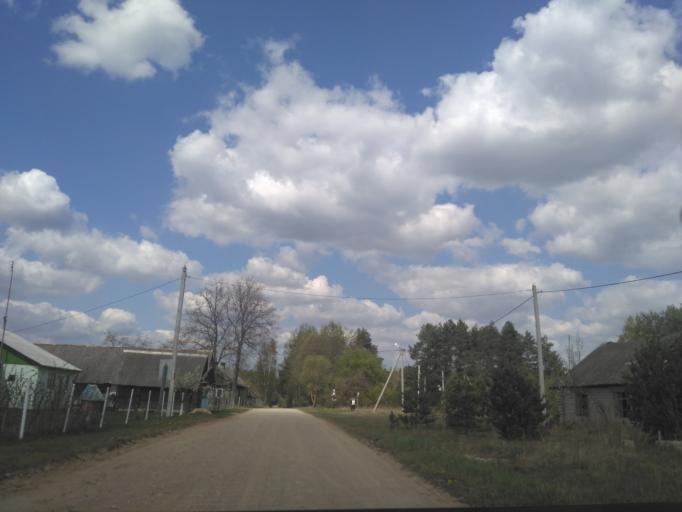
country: BY
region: Minsk
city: Il'ya
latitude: 54.2821
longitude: 27.3004
